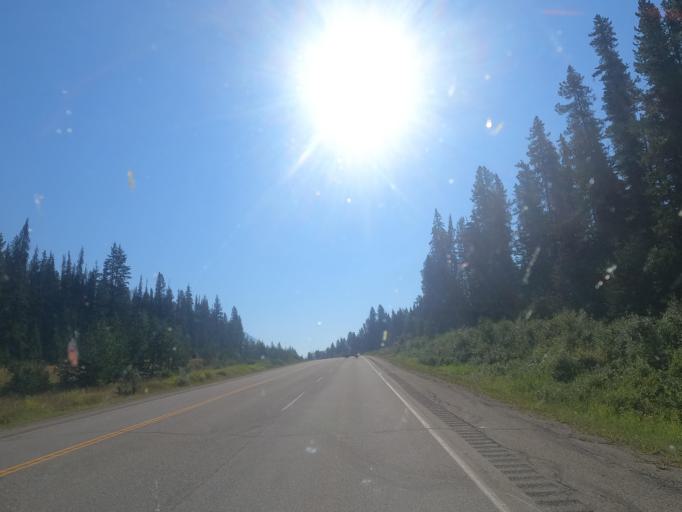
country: CA
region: Alberta
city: Grande Cache
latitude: 53.0046
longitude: -119.0513
